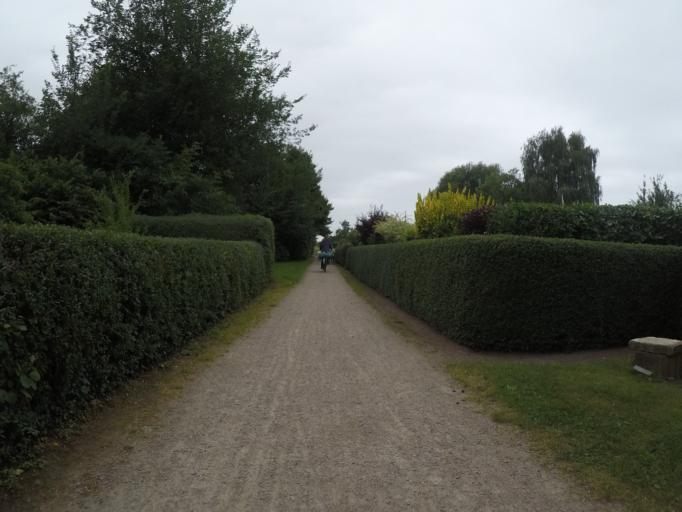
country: DE
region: Lower Saxony
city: Neu Wulmstorf
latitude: 53.5288
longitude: 9.8449
